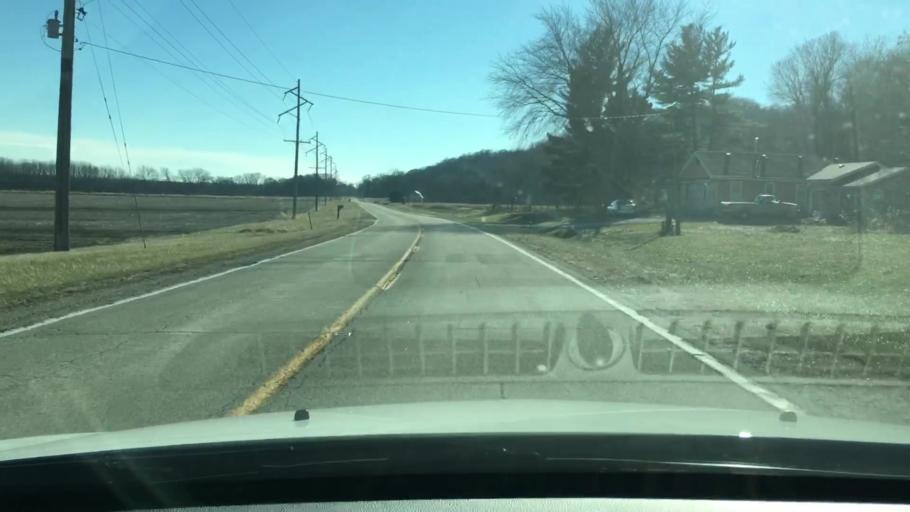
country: US
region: Illinois
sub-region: Fulton County
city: Astoria
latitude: 40.2142
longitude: -90.2079
